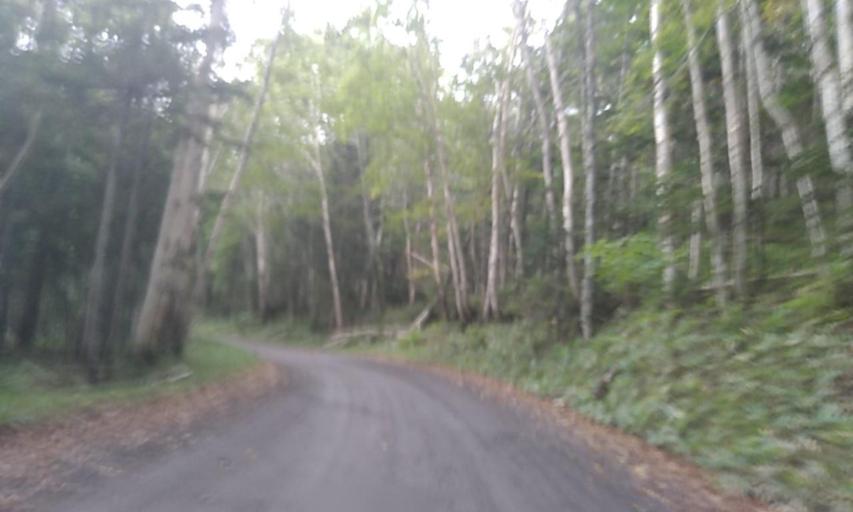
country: JP
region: Hokkaido
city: Abashiri
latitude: 43.6562
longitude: 144.5491
